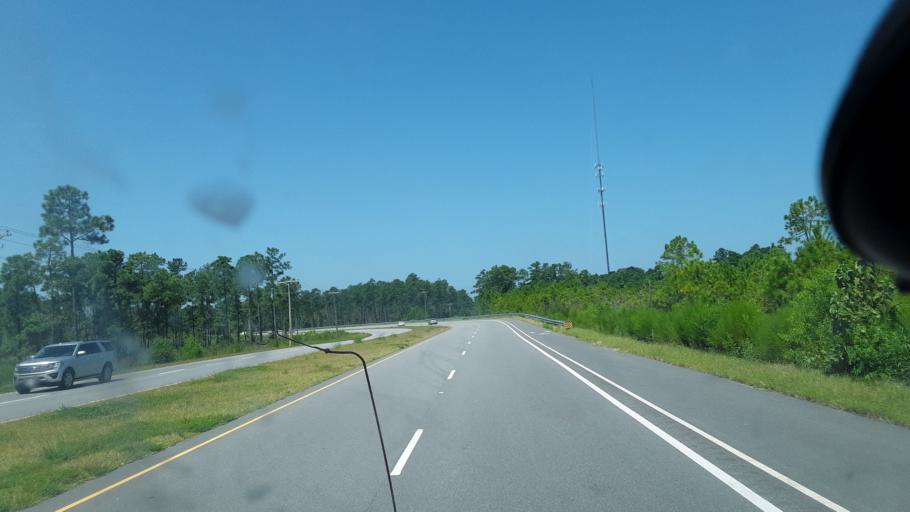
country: US
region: South Carolina
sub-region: Horry County
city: Forestbrook
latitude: 33.8158
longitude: -78.9034
